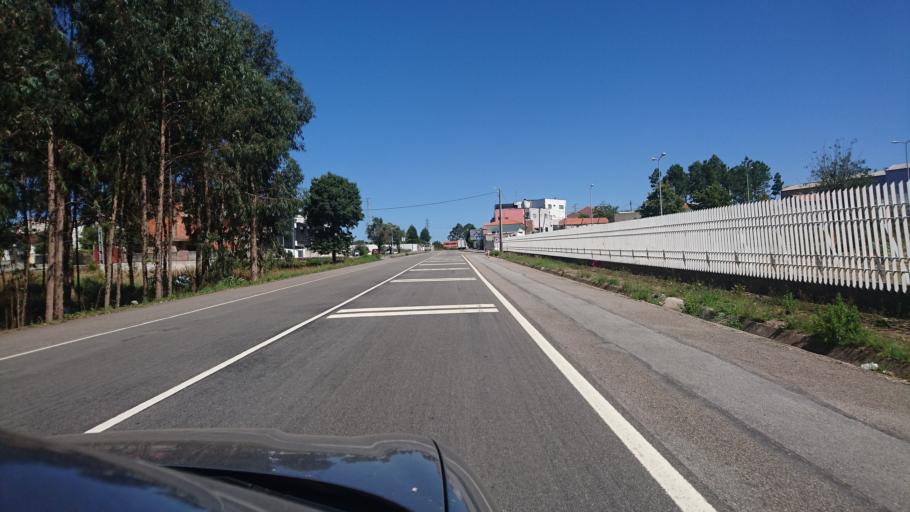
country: PT
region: Aveiro
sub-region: Santa Maria da Feira
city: Rio Meao
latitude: 40.9558
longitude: -8.5880
